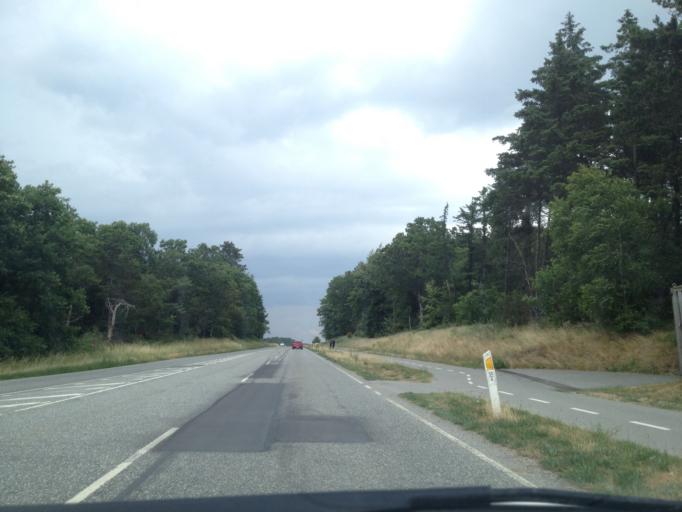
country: DK
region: Central Jutland
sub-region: Syddjurs Kommune
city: Ebeltoft
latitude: 56.1708
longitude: 10.6701
